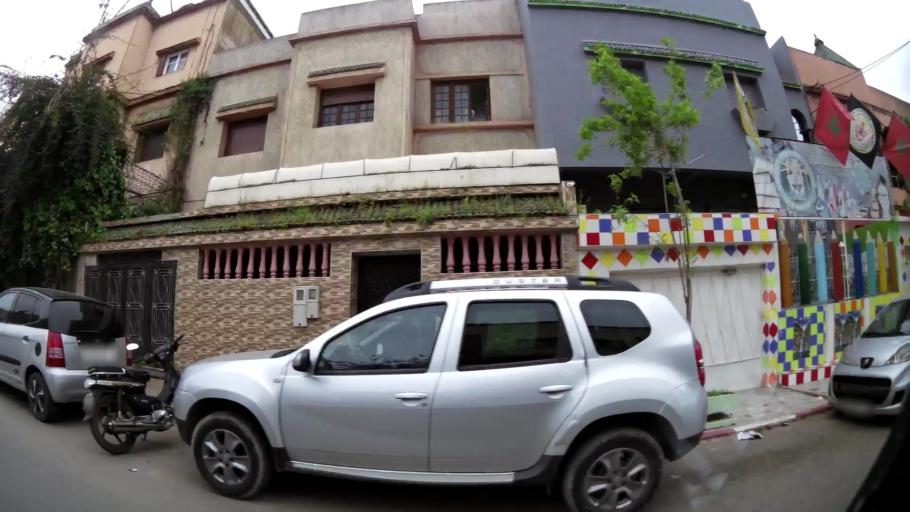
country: MA
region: Grand Casablanca
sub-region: Mediouna
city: Tit Mellil
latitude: 33.5630
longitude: -7.5353
